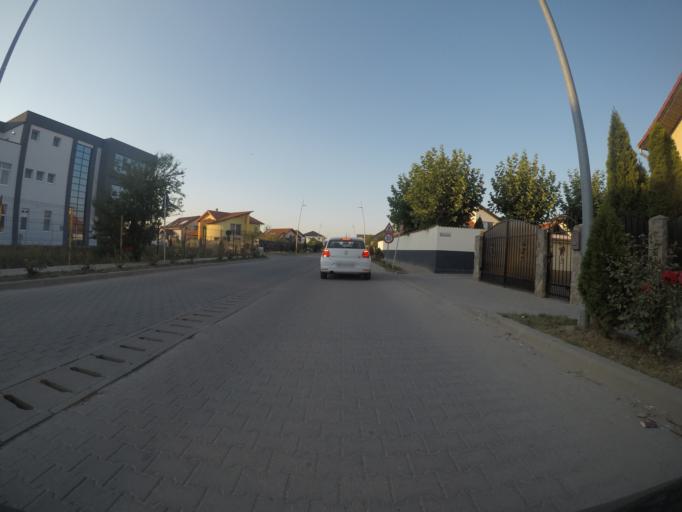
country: RO
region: Sibiu
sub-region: Comuna Selimbar
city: Selimbar
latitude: 45.7740
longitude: 24.1801
